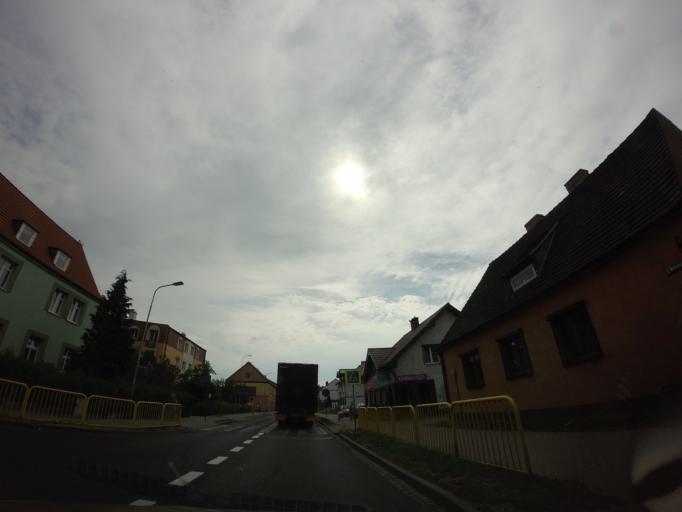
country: PL
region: West Pomeranian Voivodeship
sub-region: Powiat walecki
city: Miroslawiec
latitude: 53.3424
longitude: 16.0903
